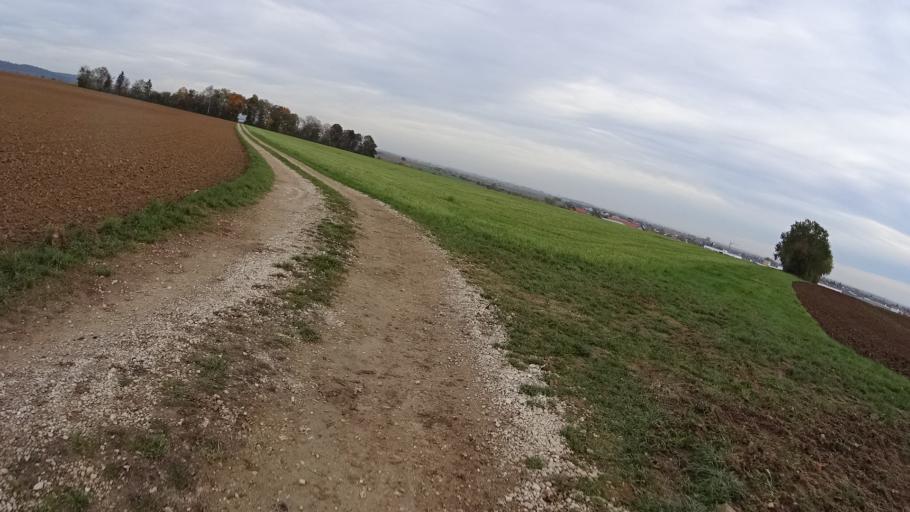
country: DE
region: Bavaria
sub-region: Upper Bavaria
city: Eitensheim
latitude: 48.8333
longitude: 11.3095
